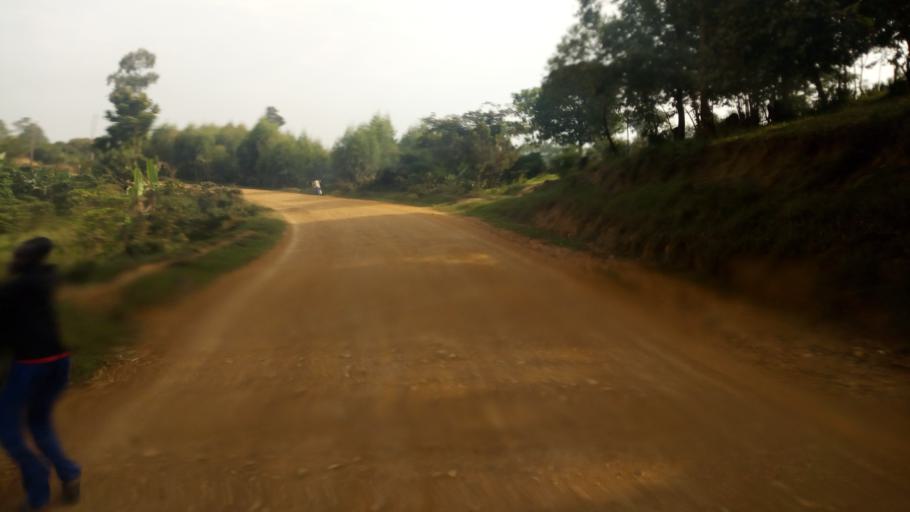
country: UG
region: Western Region
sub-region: Kanungu District
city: Ntungamo
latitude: -0.8356
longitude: 29.6809
